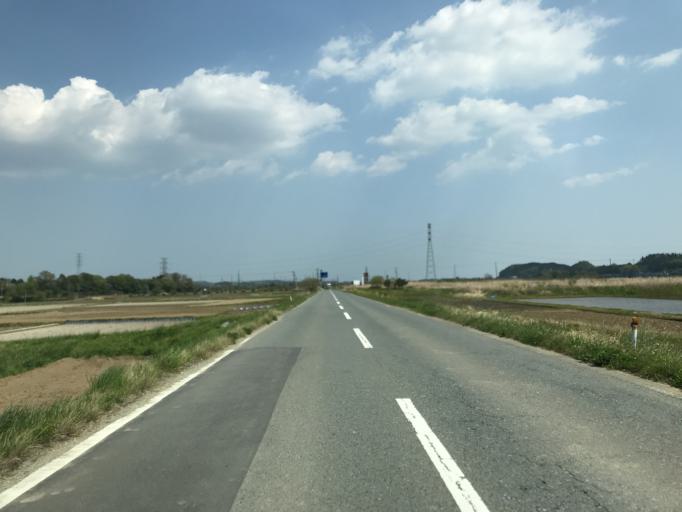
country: JP
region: Ibaraki
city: Kitaibaraki
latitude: 36.9244
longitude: 140.7473
